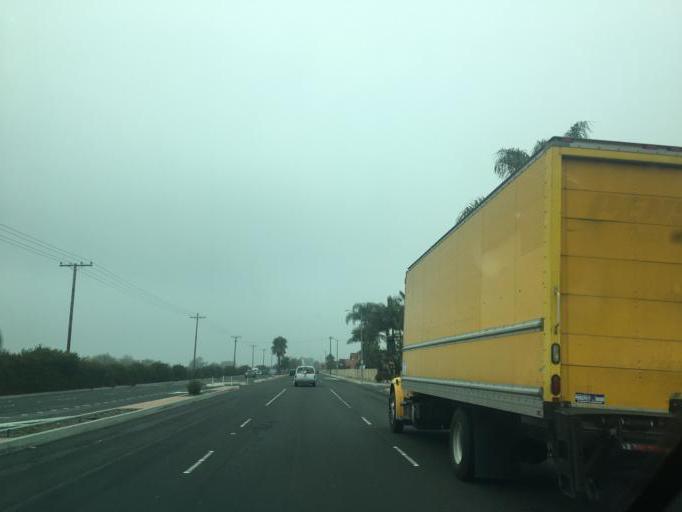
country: US
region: California
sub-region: Orange County
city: Westminster
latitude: 33.7621
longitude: -118.0425
